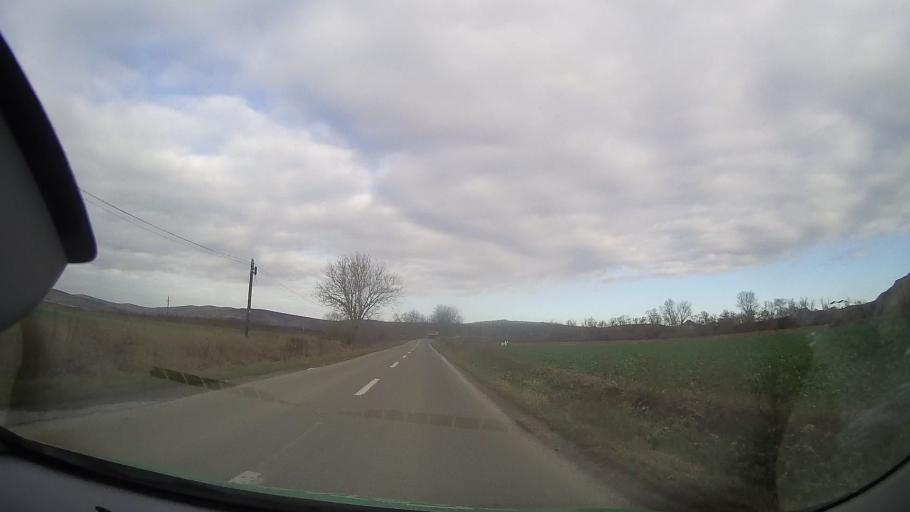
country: RO
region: Mures
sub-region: Comuna Iernut
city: Iernut
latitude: 46.4670
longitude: 24.2183
